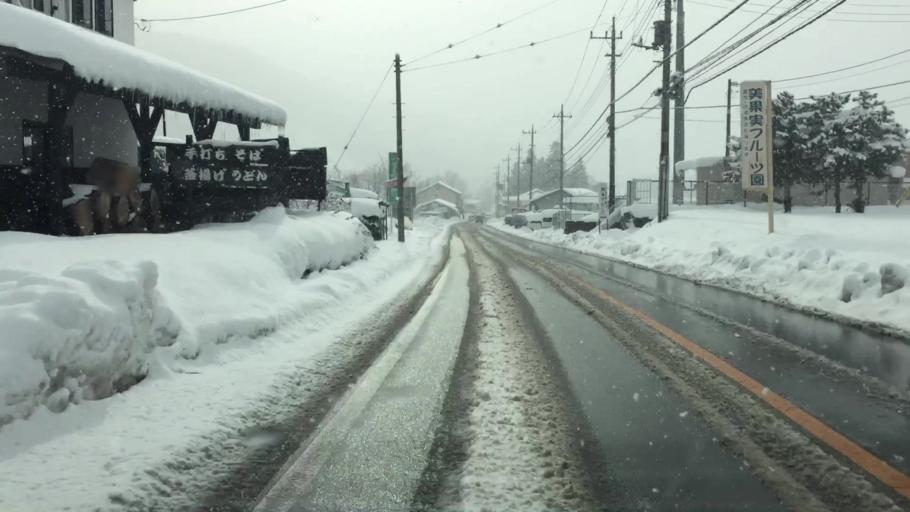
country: JP
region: Gunma
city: Numata
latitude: 36.7127
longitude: 139.0655
